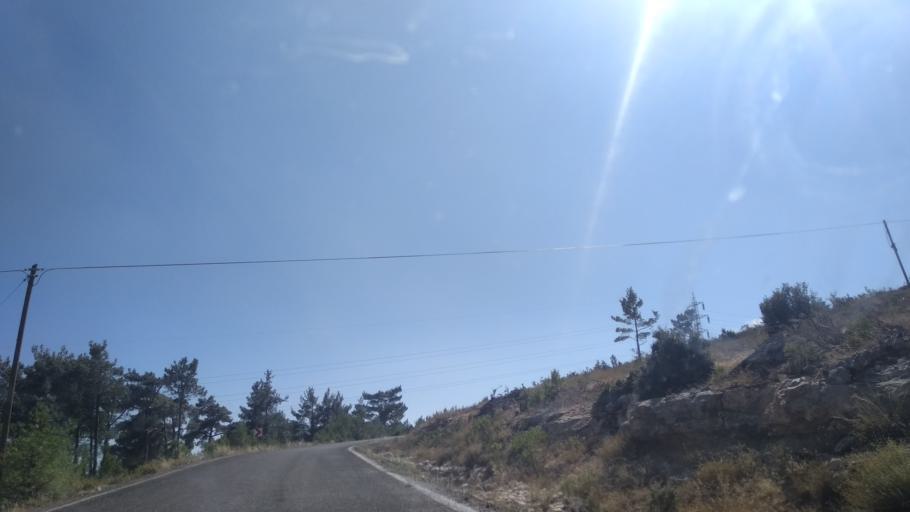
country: TR
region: Mersin
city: Gulnar
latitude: 36.3065
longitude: 33.4508
